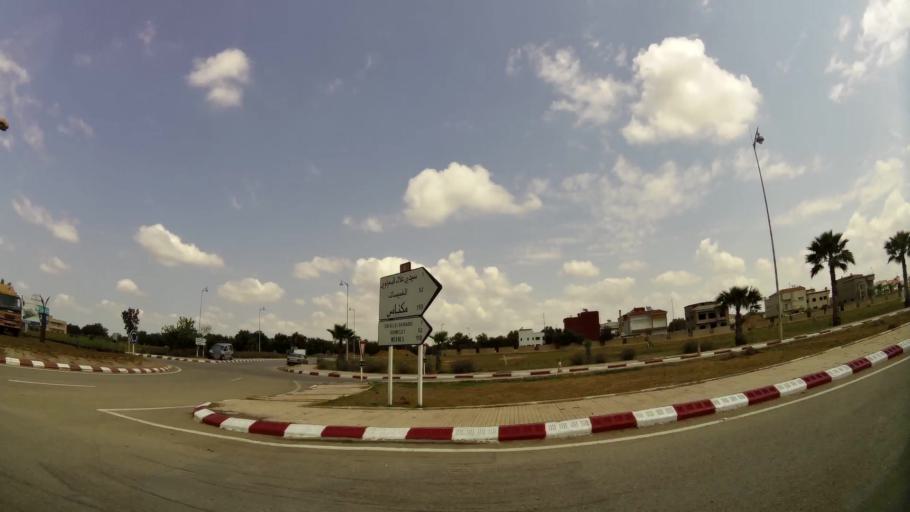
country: MA
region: Gharb-Chrarda-Beni Hssen
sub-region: Kenitra Province
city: Kenitra
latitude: 34.0130
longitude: -6.5398
